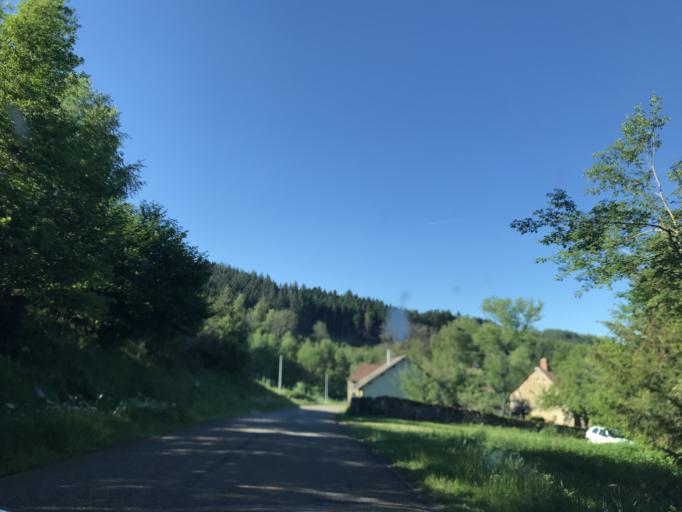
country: FR
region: Auvergne
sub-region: Departement du Puy-de-Dome
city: Job
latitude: 45.6065
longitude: 3.6562
